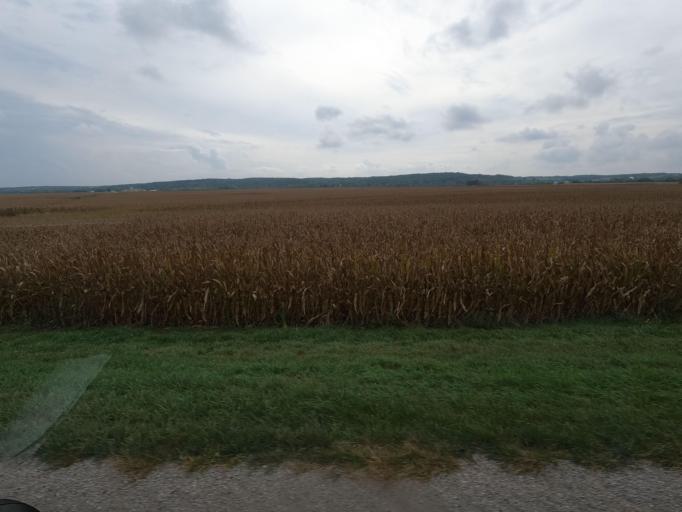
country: US
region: Iowa
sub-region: Wapello County
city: Ottumwa
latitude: 40.9005
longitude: -92.1936
